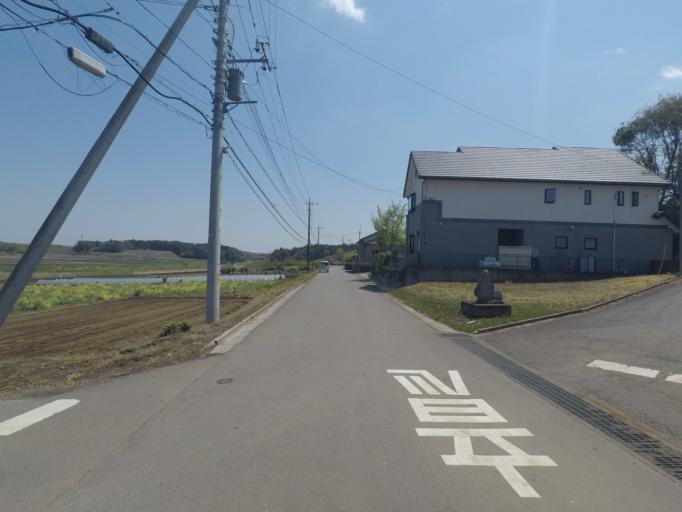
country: JP
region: Ibaraki
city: Ushiku
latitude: 36.0191
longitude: 140.0868
